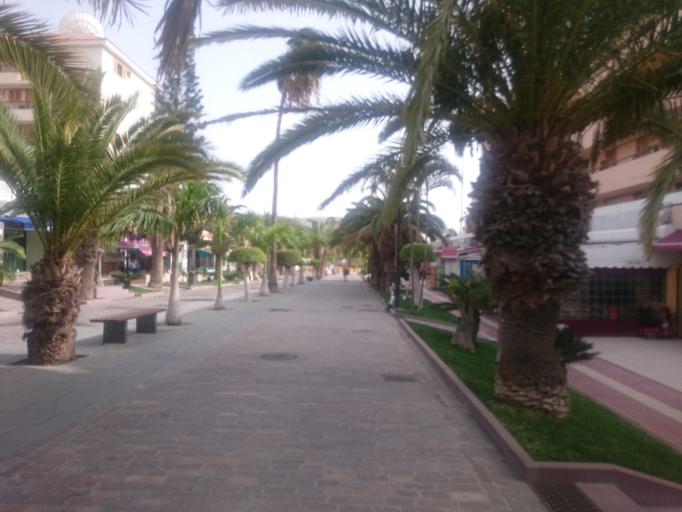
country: ES
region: Canary Islands
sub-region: Provincia de Santa Cruz de Tenerife
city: Playa de las Americas
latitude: 28.0513
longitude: -16.7161
